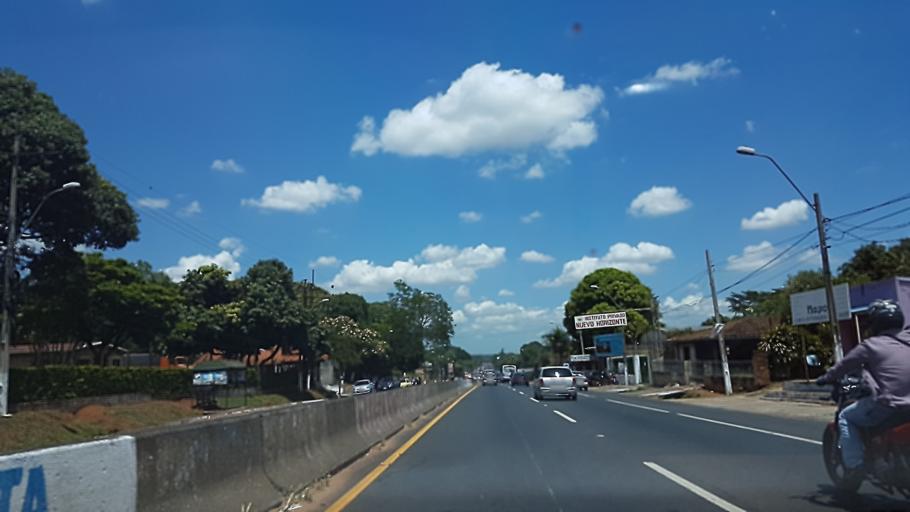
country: PY
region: Central
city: Capiata
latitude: -25.3491
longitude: -57.4563
